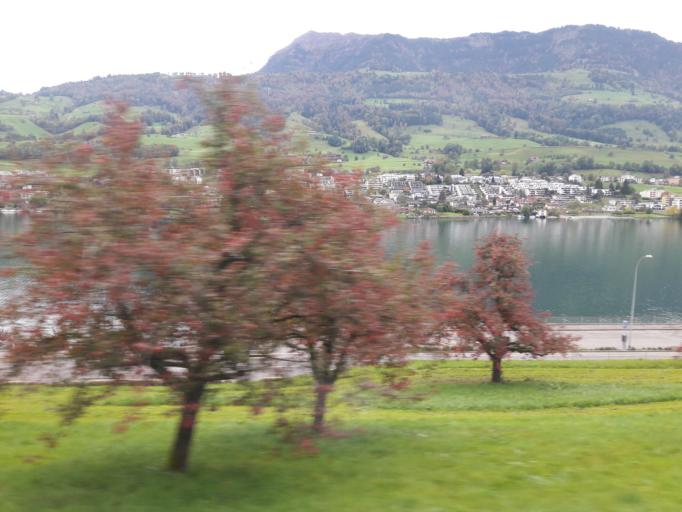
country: CH
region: Schwyz
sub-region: Bezirk Kuessnacht
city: Kussnacht
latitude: 47.0787
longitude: 8.4294
